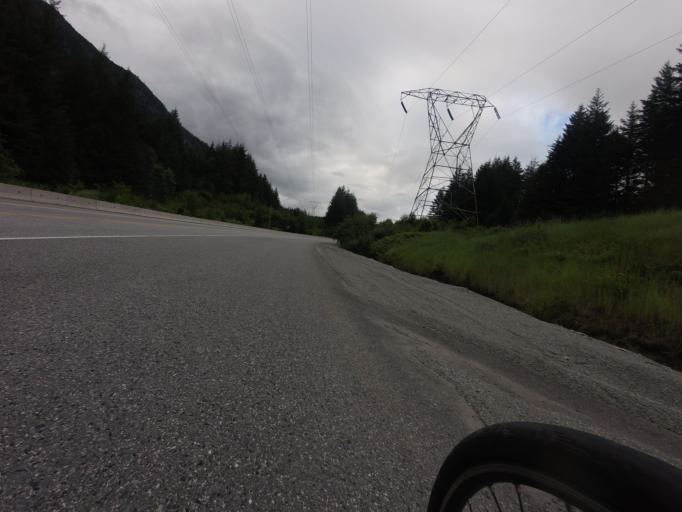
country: CA
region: British Columbia
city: Pemberton
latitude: 50.2866
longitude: -122.8475
